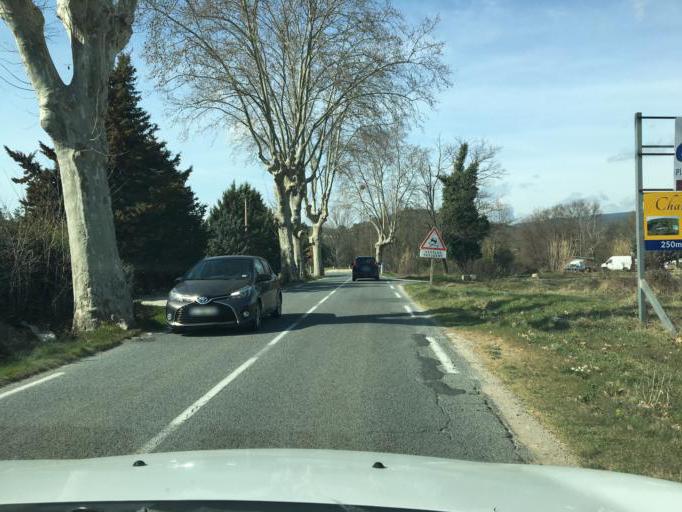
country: FR
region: Provence-Alpes-Cote d'Azur
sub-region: Departement du Var
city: Flayosc
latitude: 43.5338
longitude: 6.4099
